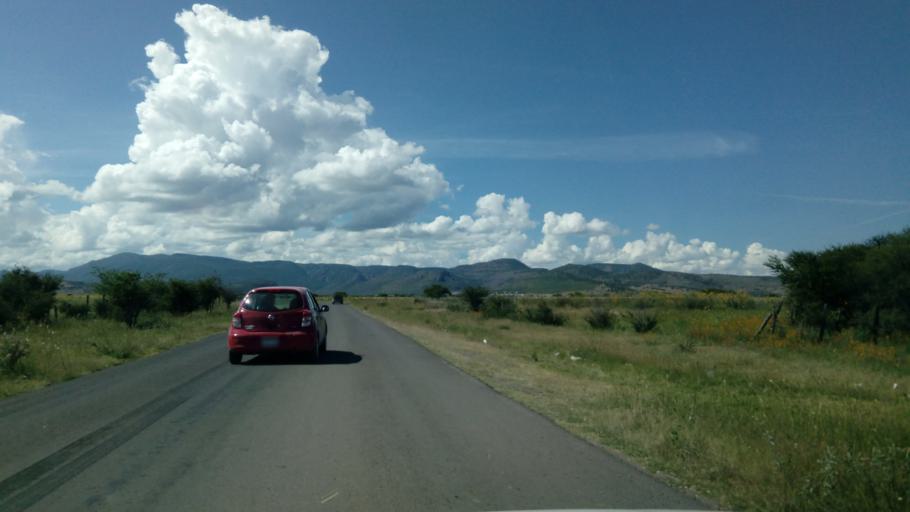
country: MX
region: Durango
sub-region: Durango
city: Jose Refugio Salcido
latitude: 23.8631
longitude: -104.4727
